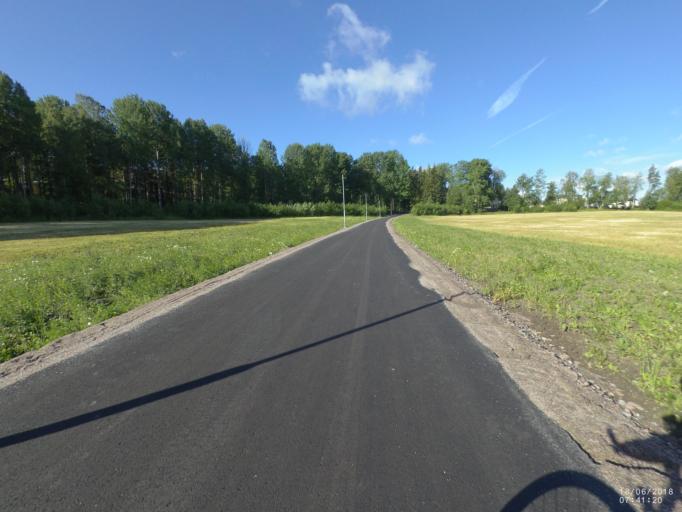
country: SE
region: Soedermanland
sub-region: Nykopings Kommun
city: Nykoping
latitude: 58.7627
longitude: 17.0615
